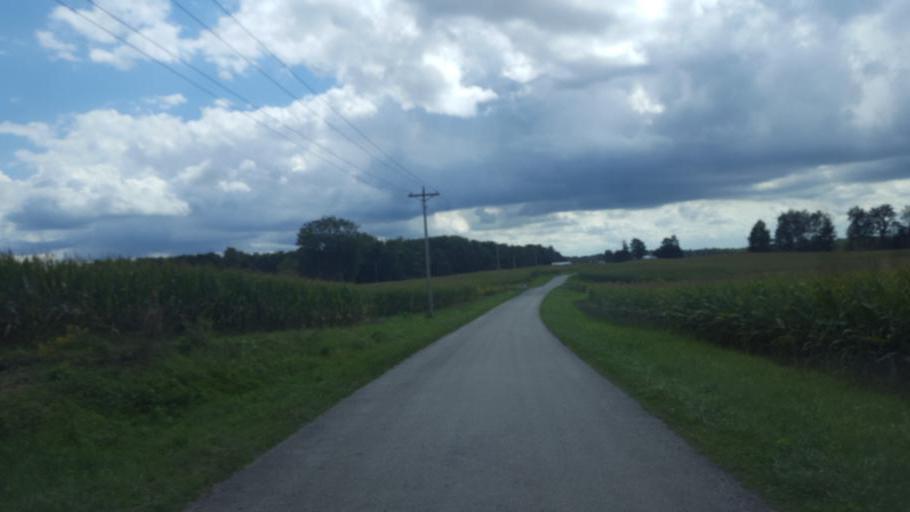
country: US
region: Ohio
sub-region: Huron County
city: Plymouth
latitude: 41.0915
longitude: -82.6304
